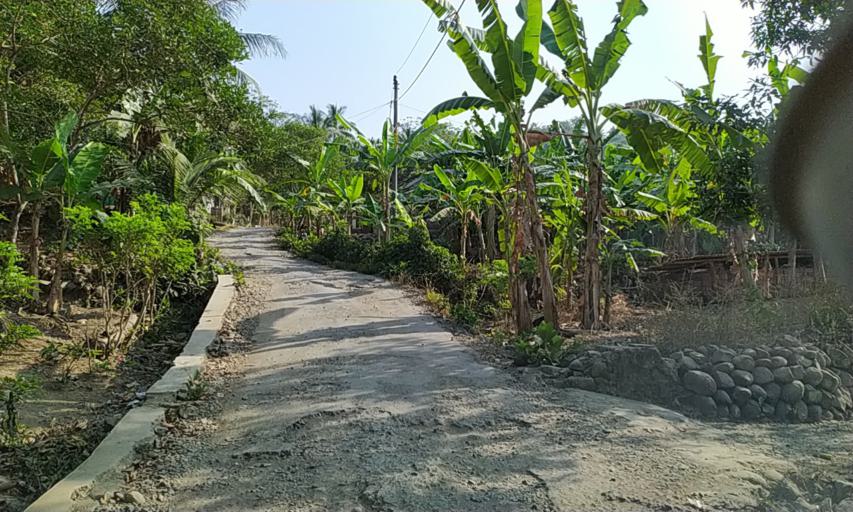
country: ID
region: Central Java
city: Jambuluwuk
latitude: -7.3246
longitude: 108.8749
